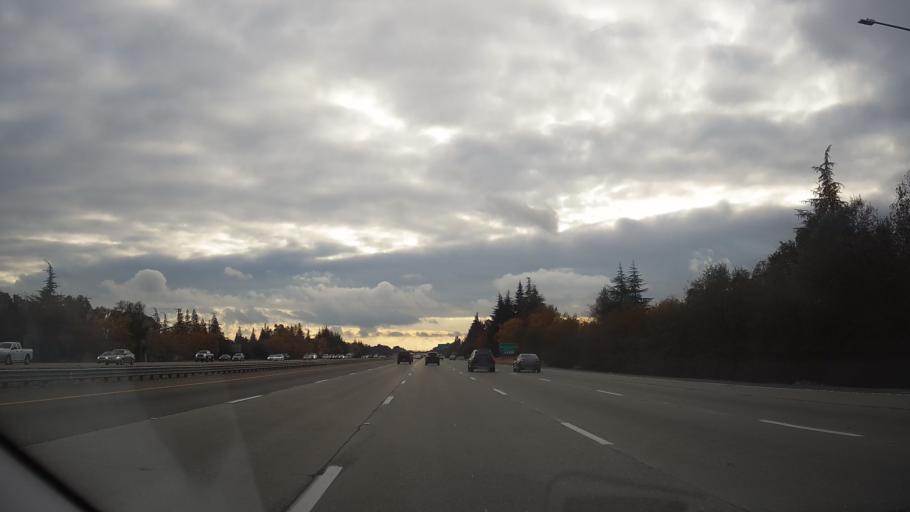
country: US
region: California
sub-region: Sacramento County
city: Antelope
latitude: 38.6919
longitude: -121.3268
